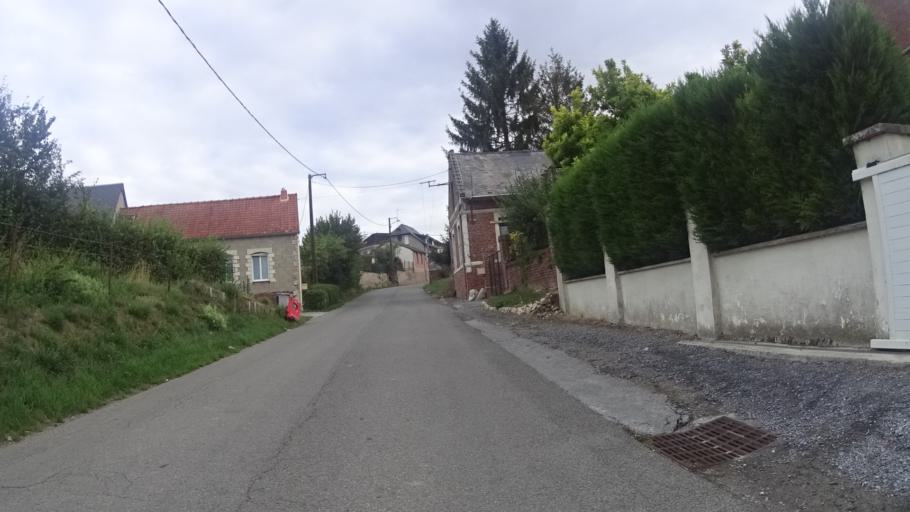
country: FR
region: Picardie
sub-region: Departement de l'Aisne
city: Guise
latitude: 49.9366
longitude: 3.5826
